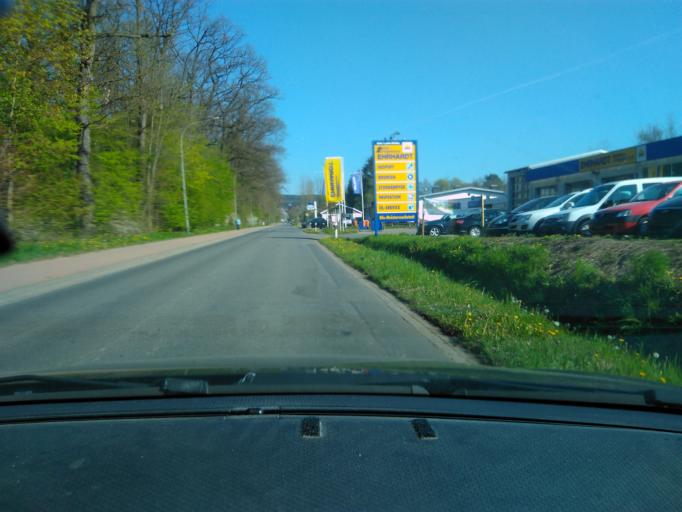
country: DE
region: Lower Saxony
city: Osterode am Harz
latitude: 51.7216
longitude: 10.2645
